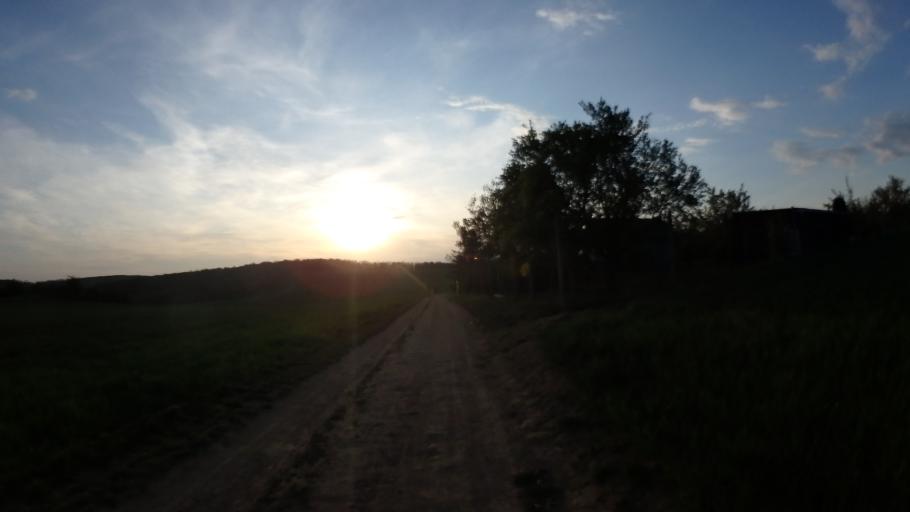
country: CZ
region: South Moravian
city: Ostopovice
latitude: 49.1494
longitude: 16.5453
